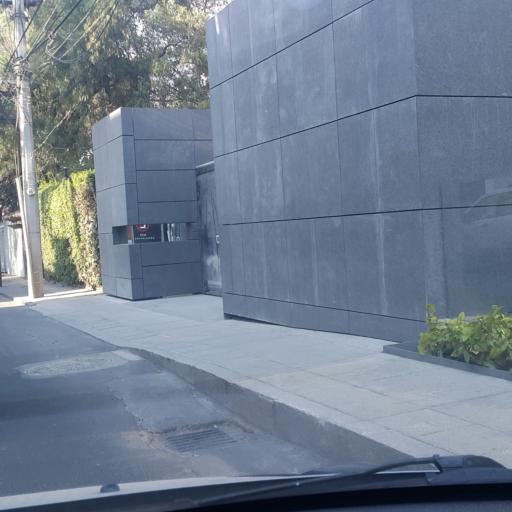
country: MX
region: Mexico City
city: Miguel Hidalgo
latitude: 19.4291
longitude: -99.2081
